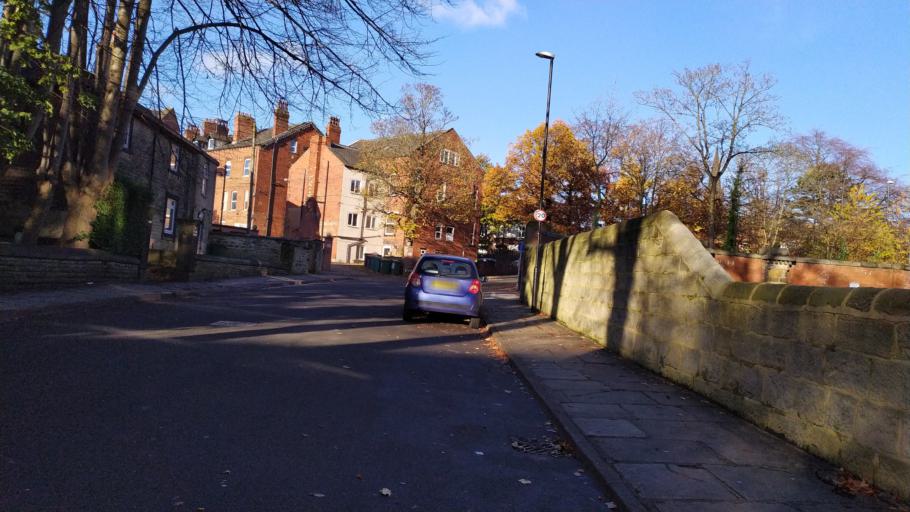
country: GB
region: England
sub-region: City and Borough of Leeds
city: Leeds
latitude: 53.8166
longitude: -1.5778
